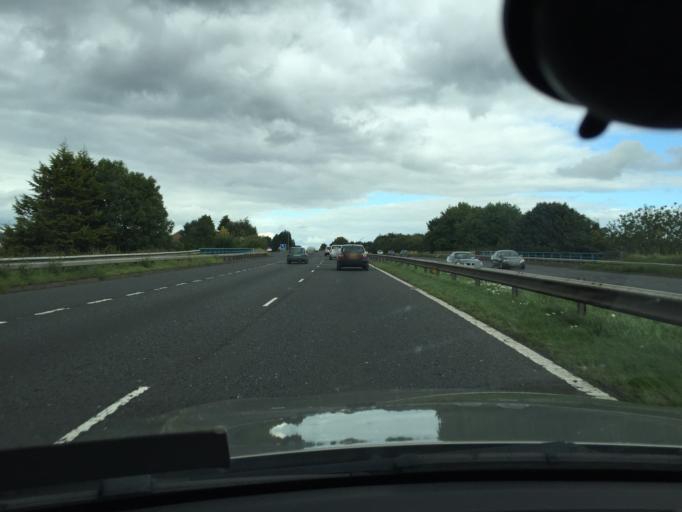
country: GB
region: Northern Ireland
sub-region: Lisburn District
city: Lisburn
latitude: 54.5024
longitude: -6.0333
